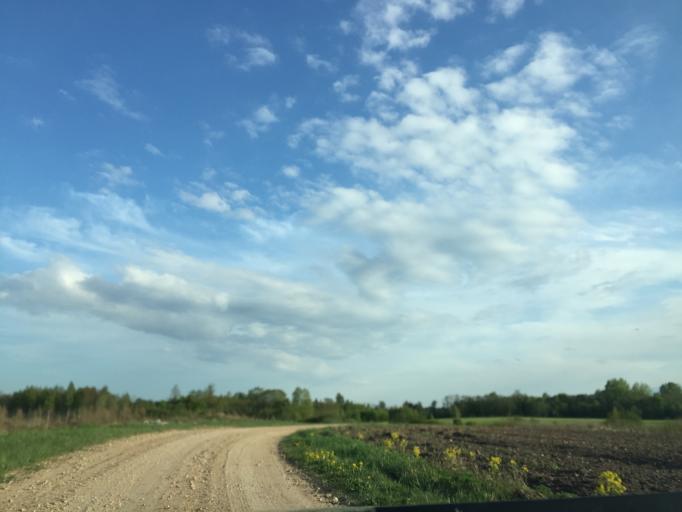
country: LV
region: Limbazu Rajons
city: Limbazi
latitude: 57.3761
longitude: 24.6384
